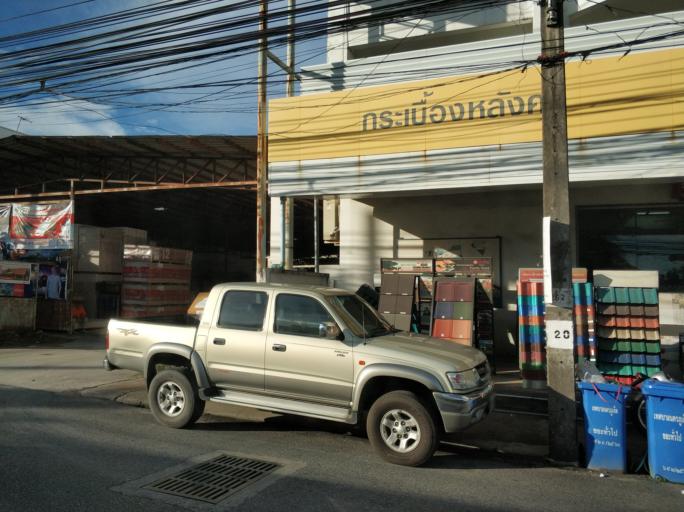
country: TH
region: Phuket
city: Ban Talat Nua
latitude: 7.8860
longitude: 98.3765
